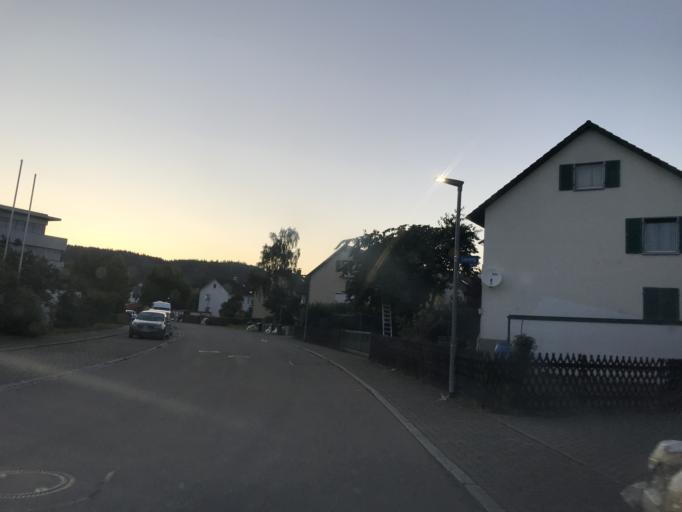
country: DE
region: Baden-Wuerttemberg
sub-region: Freiburg Region
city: Schopfheim
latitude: 47.6435
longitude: 7.8084
